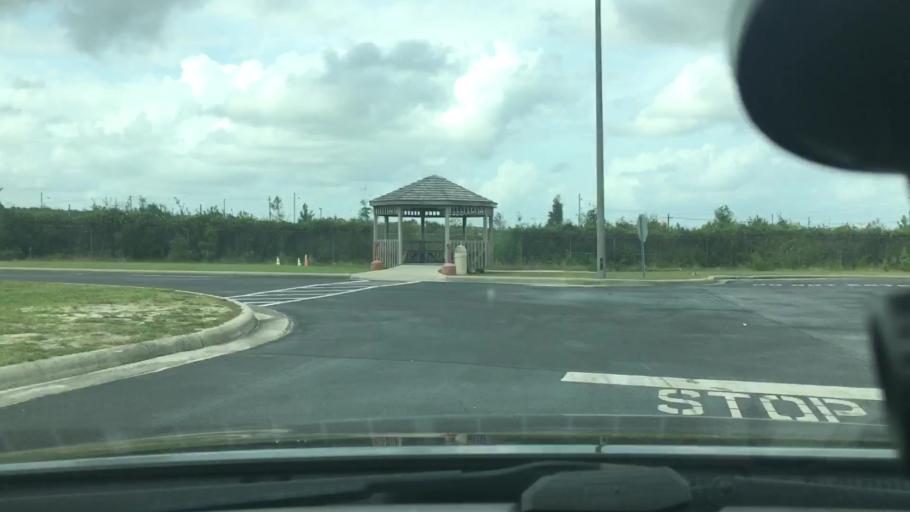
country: US
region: North Carolina
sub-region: Craven County
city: Havelock
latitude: 34.8808
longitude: -76.8995
